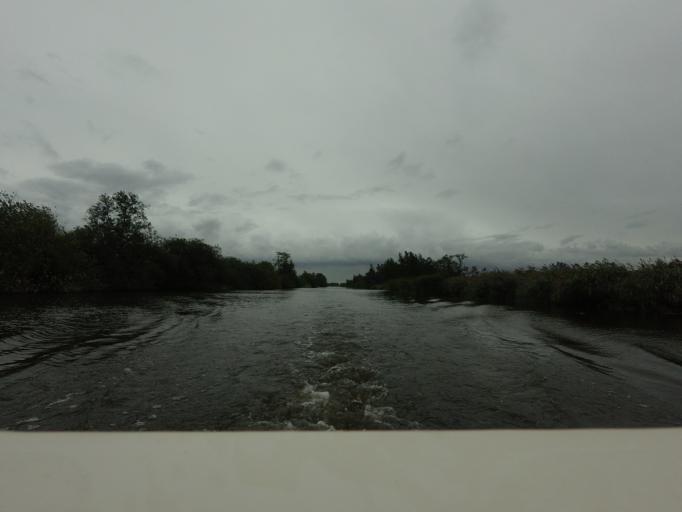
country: NL
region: Friesland
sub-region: Gemeente Boarnsterhim
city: Warten
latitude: 53.1195
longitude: 5.9306
